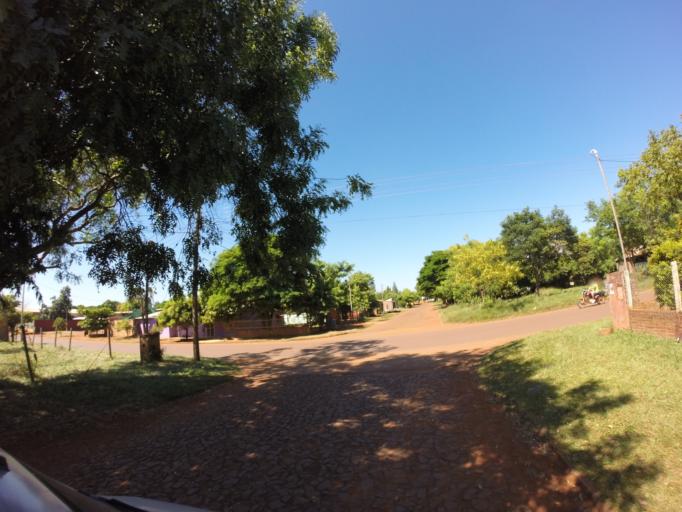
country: PY
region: Alto Parana
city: Ciudad del Este
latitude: -25.4333
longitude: -54.6468
